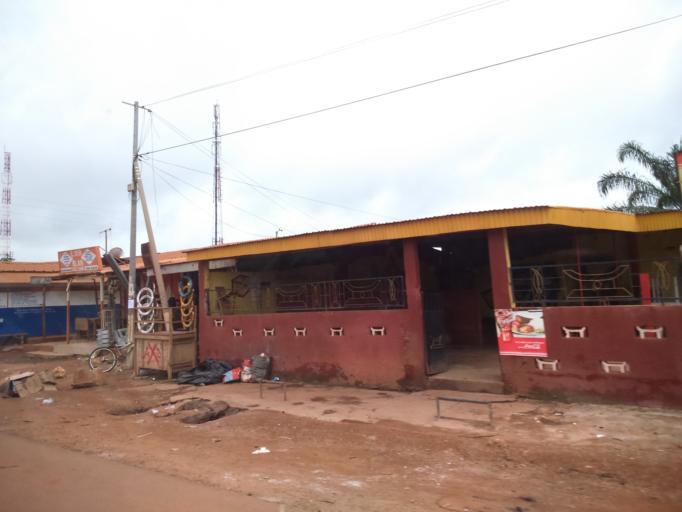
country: CI
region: Moyen-Comoe
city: Abengourou
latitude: 6.7271
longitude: -3.4974
